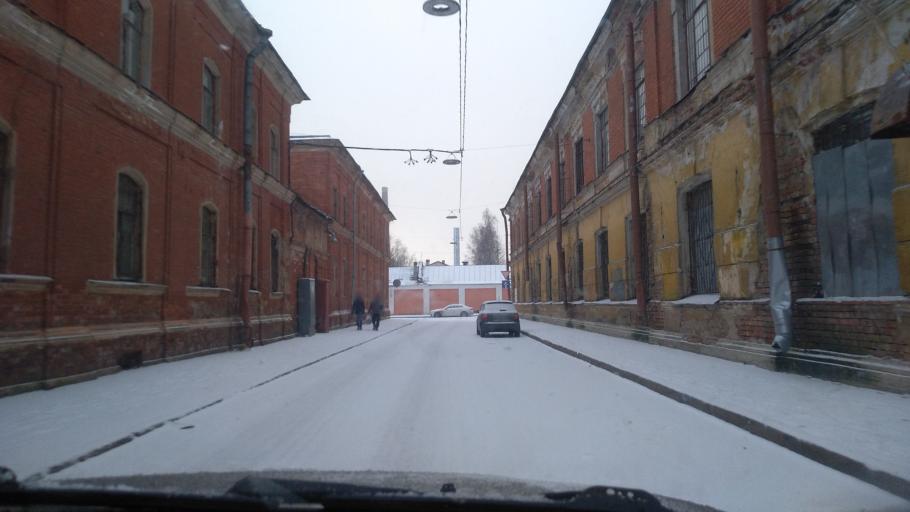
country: RU
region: St.-Petersburg
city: Kronshtadt
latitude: 59.9867
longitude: 29.7837
